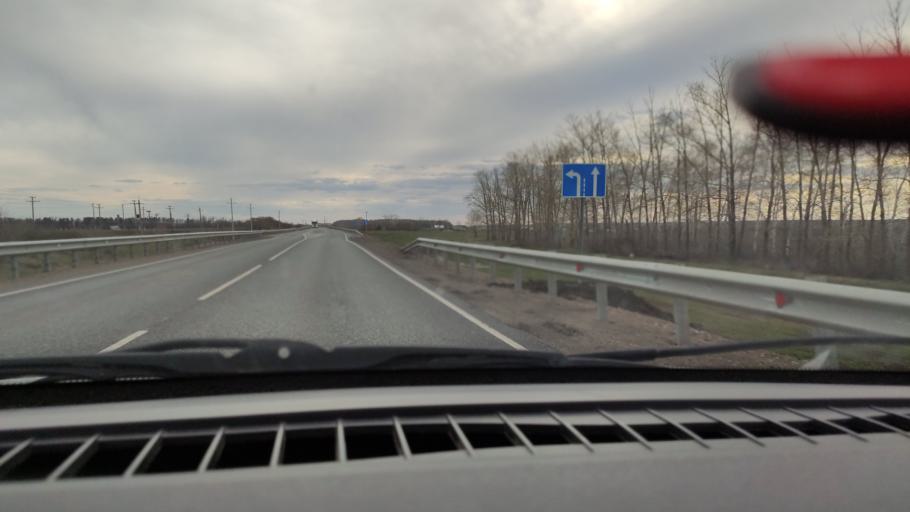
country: RU
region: Bashkortostan
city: Mayachnyy
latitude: 52.4030
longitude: 55.7188
